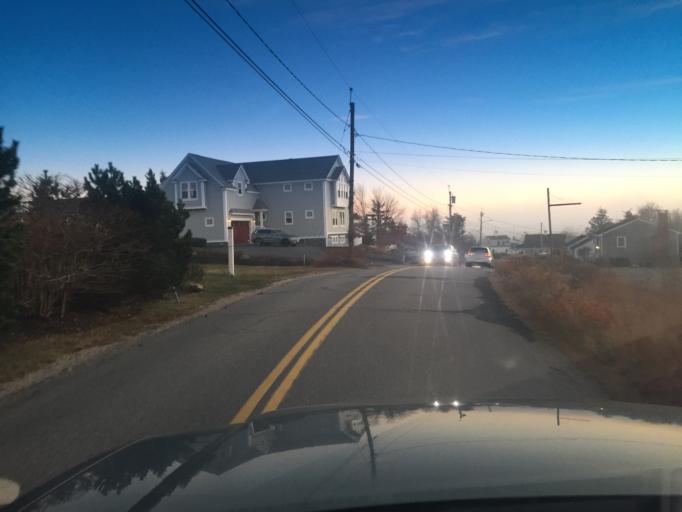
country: US
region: Maine
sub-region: York County
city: York Beach
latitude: 43.1694
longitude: -70.5955
